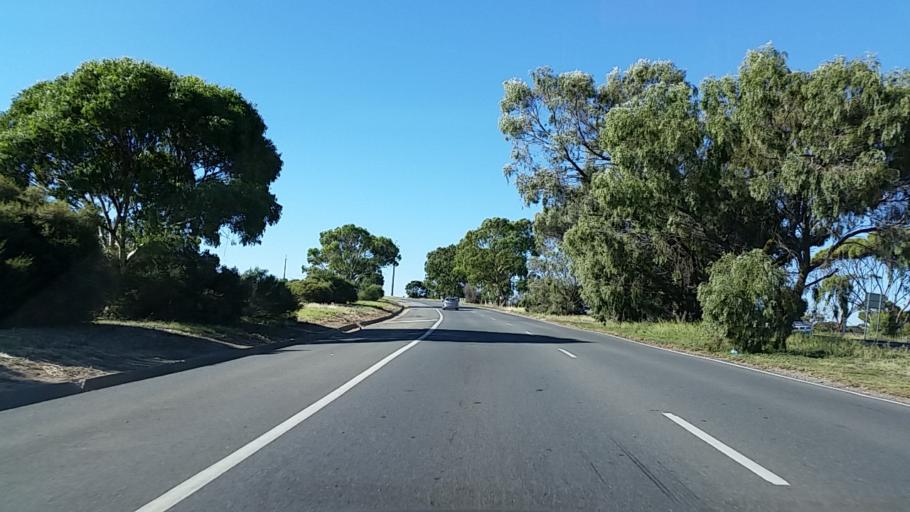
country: AU
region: South Australia
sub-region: Marion
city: Trott Park
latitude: -35.0633
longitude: 138.5342
